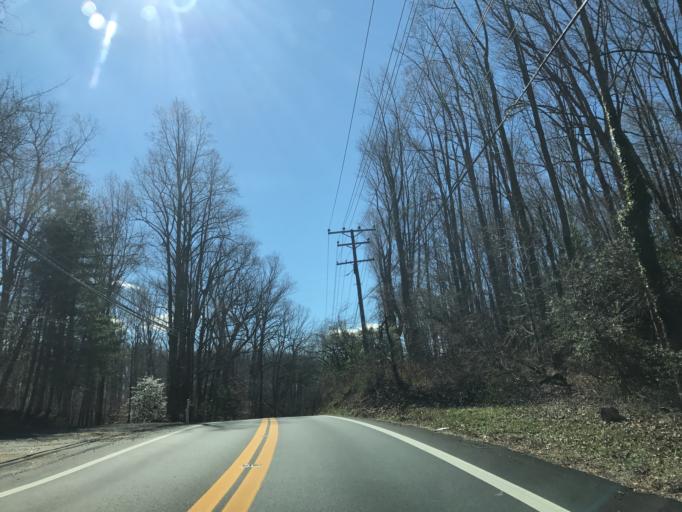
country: US
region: Maryland
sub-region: Anne Arundel County
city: Naval Academy
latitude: 39.0131
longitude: -76.4730
